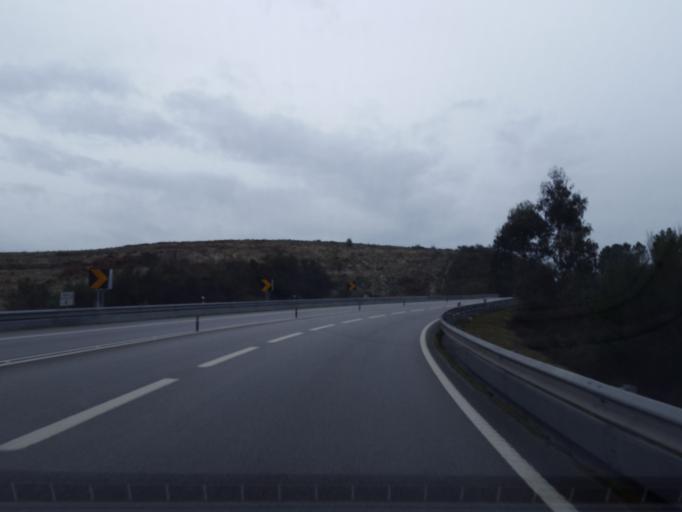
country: PT
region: Porto
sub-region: Marco de Canaveses
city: Marco de Canavezes
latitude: 41.2152
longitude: -8.1723
